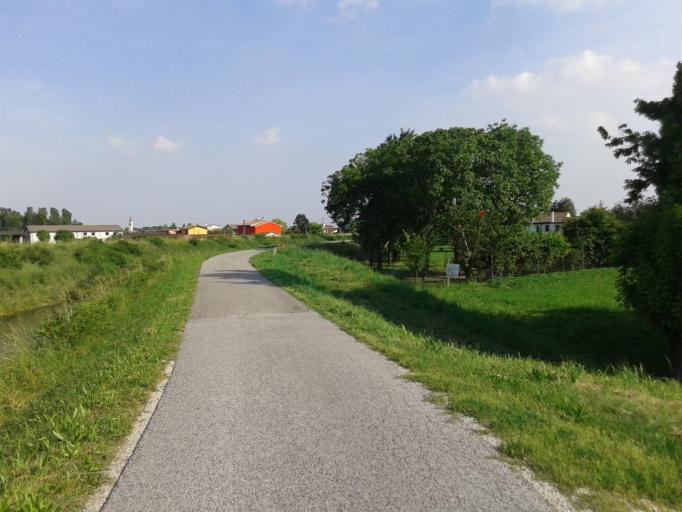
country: IT
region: Veneto
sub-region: Provincia di Padova
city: Loreggiola
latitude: 45.6022
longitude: 11.9328
